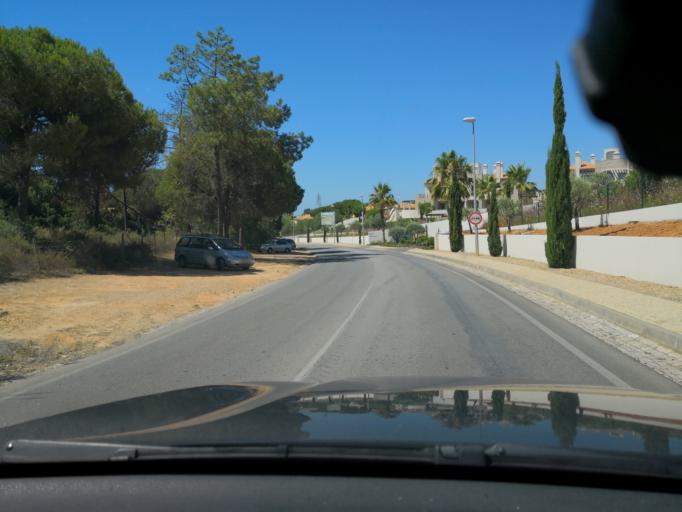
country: PT
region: Faro
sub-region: Loule
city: Vilamoura
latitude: 37.0935
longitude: -8.1020
